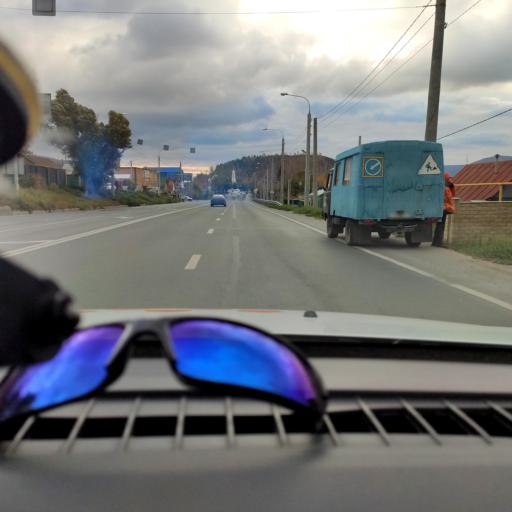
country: RU
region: Samara
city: Volzhskiy
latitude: 53.4311
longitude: 50.1181
